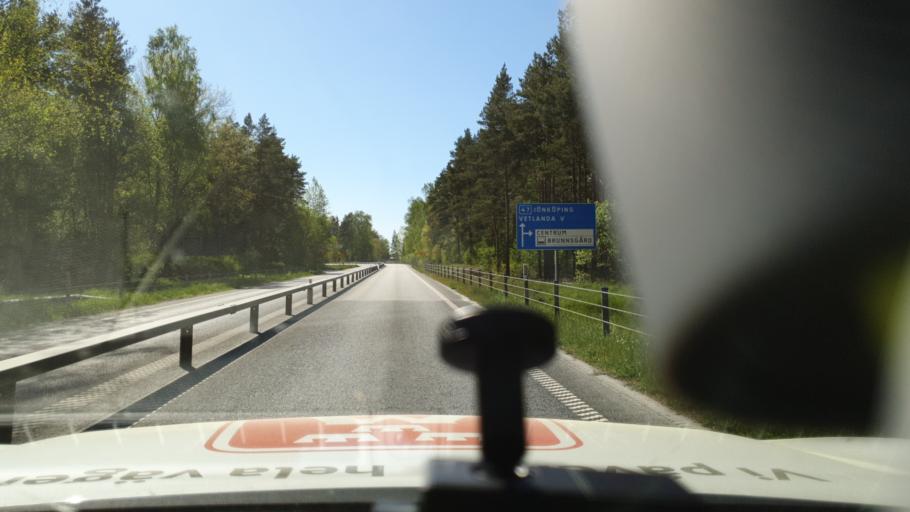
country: SE
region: Joenkoeping
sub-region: Vetlanda Kommun
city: Vetlanda
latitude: 57.4239
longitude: 15.1234
